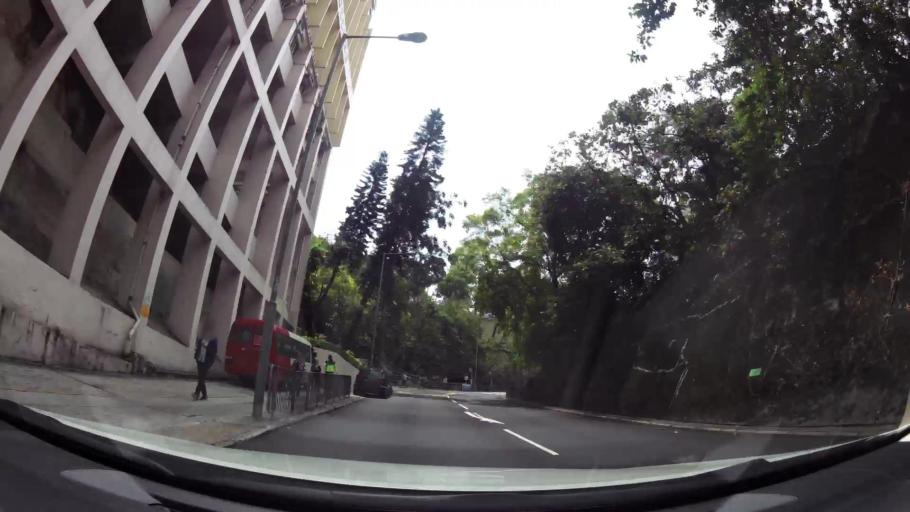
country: HK
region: Wanchai
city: Wan Chai
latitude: 22.2861
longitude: 114.1958
